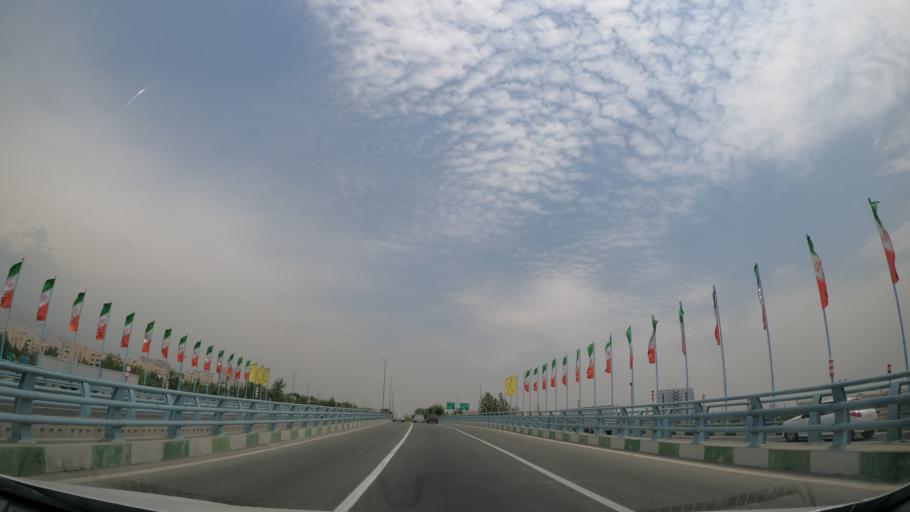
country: IR
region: Tehran
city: Shahr-e Qods
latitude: 35.7390
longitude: 51.2539
